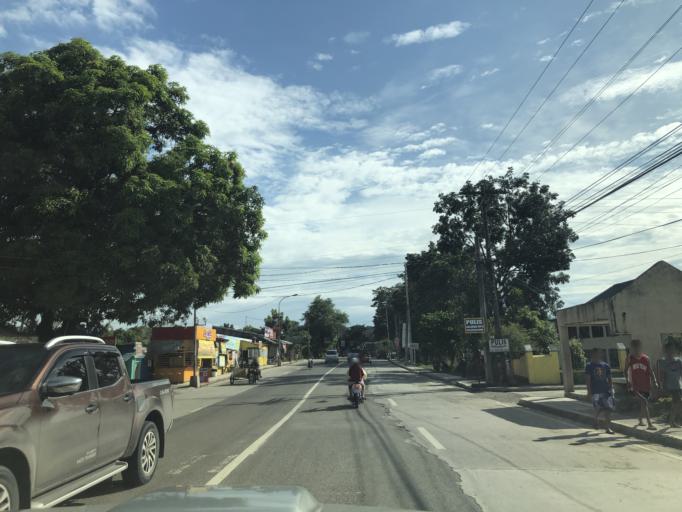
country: PH
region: Western Visayas
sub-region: Province of Iloilo
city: Maribong
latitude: 11.1221
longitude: 122.5388
